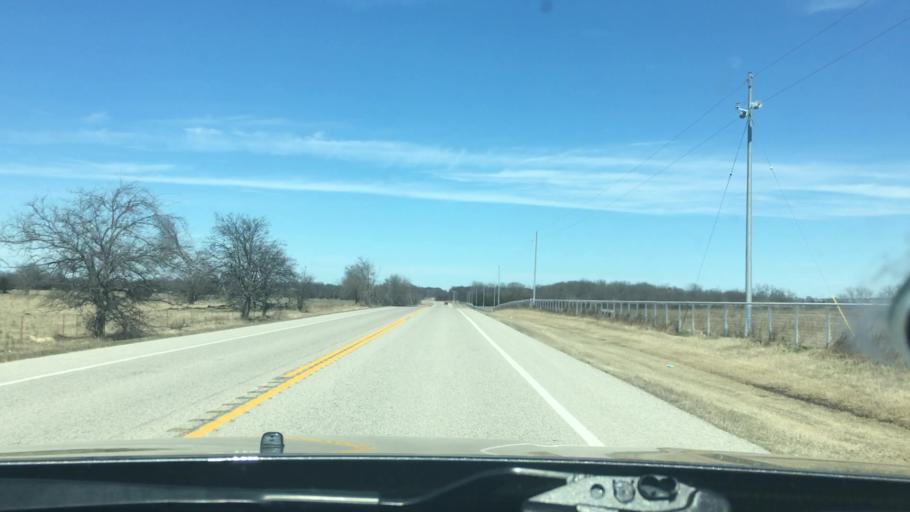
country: US
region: Oklahoma
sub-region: Murray County
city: Sulphur
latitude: 34.3800
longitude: -96.9508
